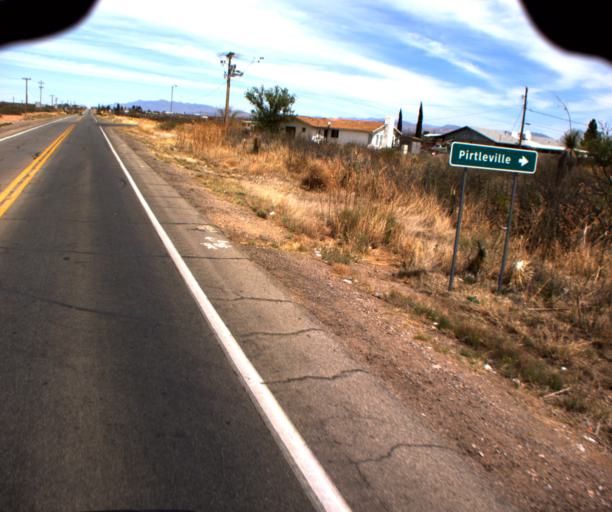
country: US
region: Arizona
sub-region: Cochise County
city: Pirtleville
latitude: 31.3575
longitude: -109.5794
